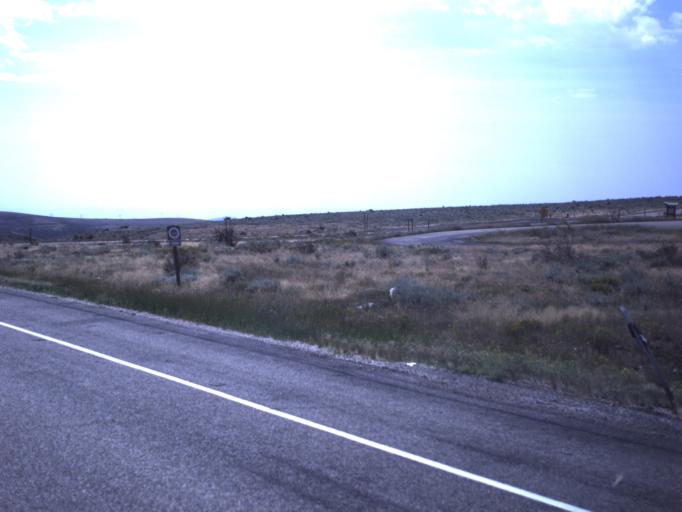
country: US
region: Utah
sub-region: Uintah County
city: Maeser
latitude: 40.6777
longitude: -109.4866
